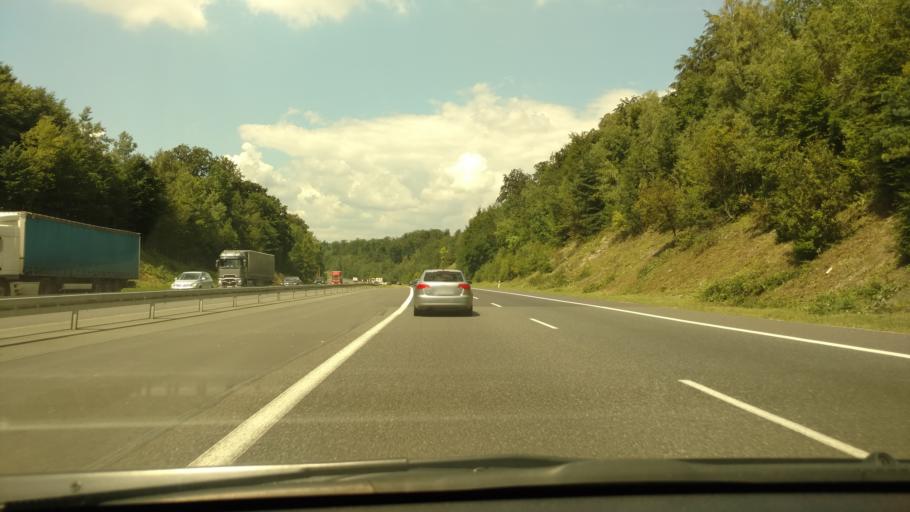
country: PL
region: Lesser Poland Voivodeship
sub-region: Powiat krakowski
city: Czulow
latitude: 50.0912
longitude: 19.6863
